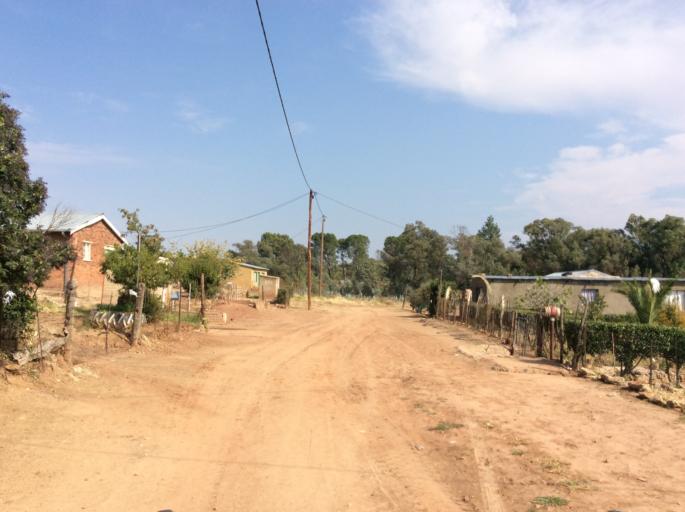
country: ZA
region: Orange Free State
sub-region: Xhariep District Municipality
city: Dewetsdorp
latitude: -29.5864
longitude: 26.6686
